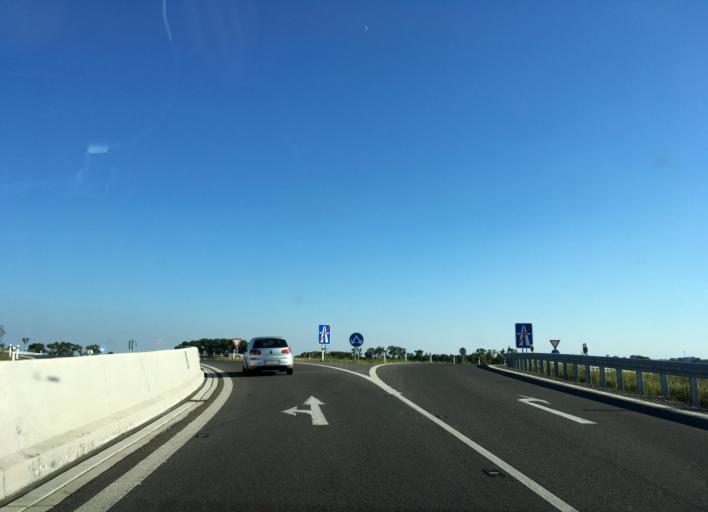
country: SK
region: Trnavsky
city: Samorin
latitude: 48.0418
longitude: 17.3375
